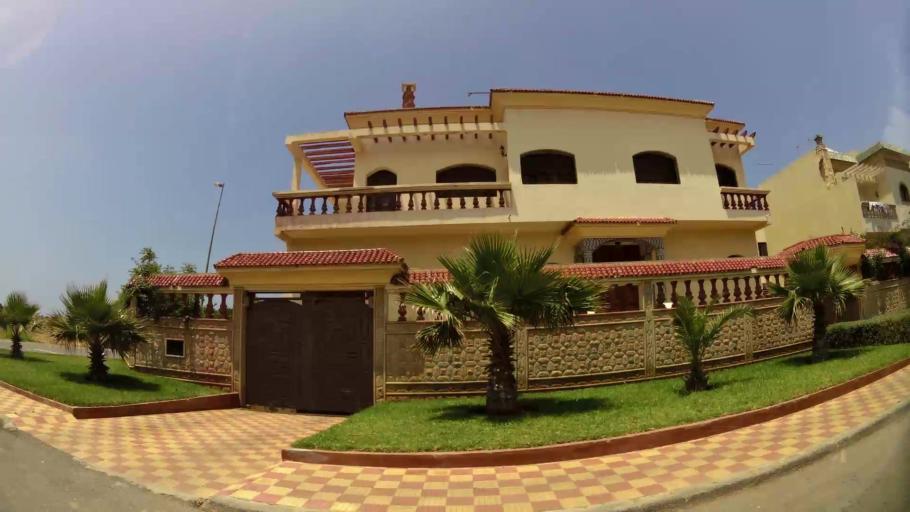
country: MA
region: Rabat-Sale-Zemmour-Zaer
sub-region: Skhirate-Temara
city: Temara
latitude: 33.9674
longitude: -6.9066
